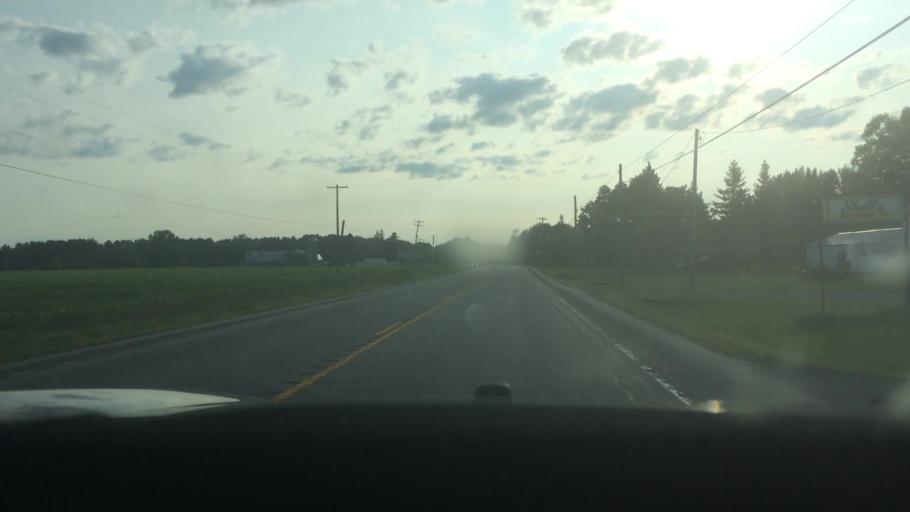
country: US
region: New York
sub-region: St. Lawrence County
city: Ogdensburg
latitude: 44.6734
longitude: -75.4173
